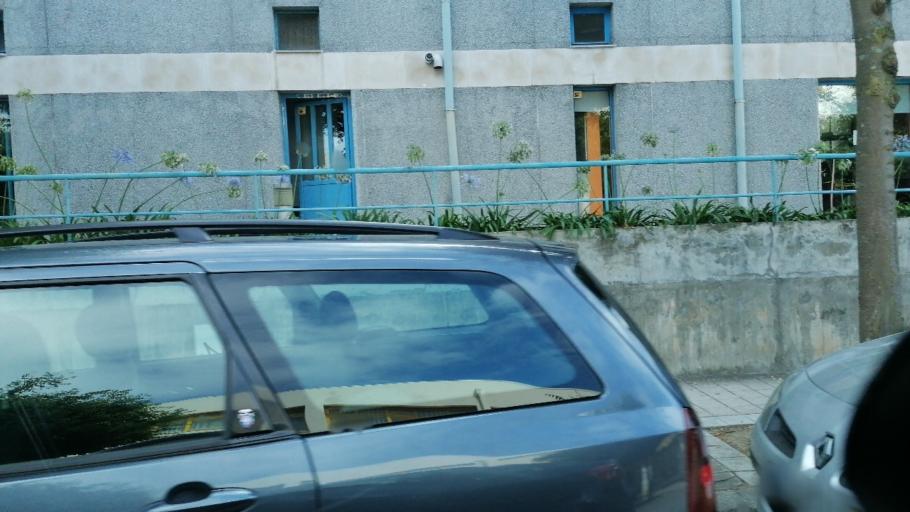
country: PT
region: Porto
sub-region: Matosinhos
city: Senhora da Hora
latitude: 41.1714
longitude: -8.6422
